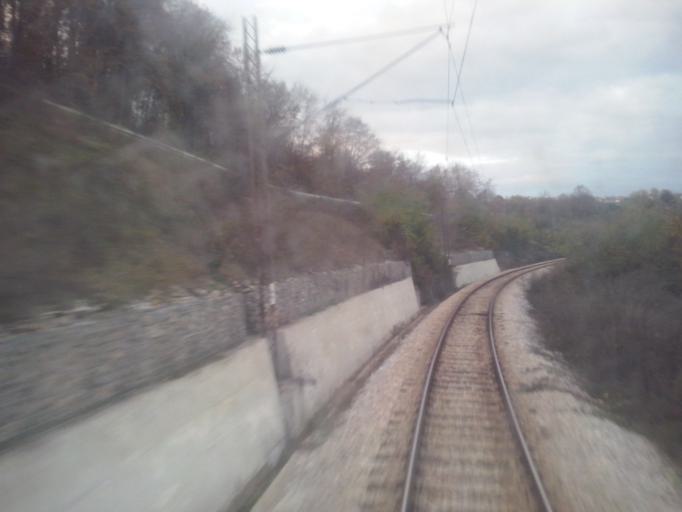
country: RS
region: Central Serbia
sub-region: Kolubarski Okrug
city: Valjevo
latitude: 44.2378
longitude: 19.8799
